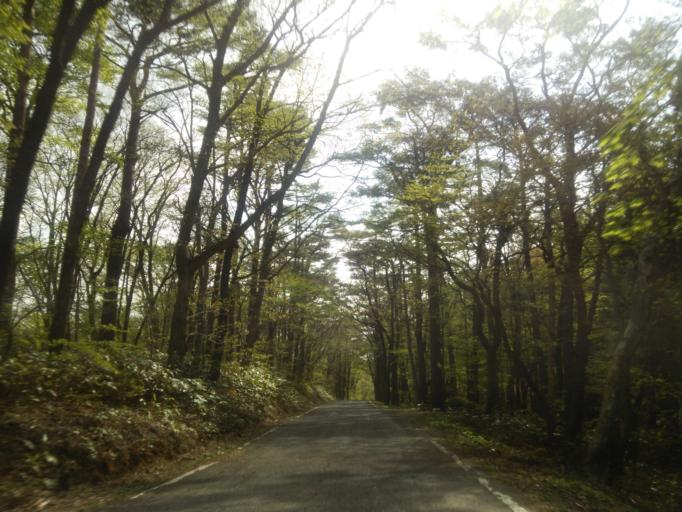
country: JP
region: Fukushima
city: Nihommatsu
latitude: 37.6411
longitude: 140.3355
